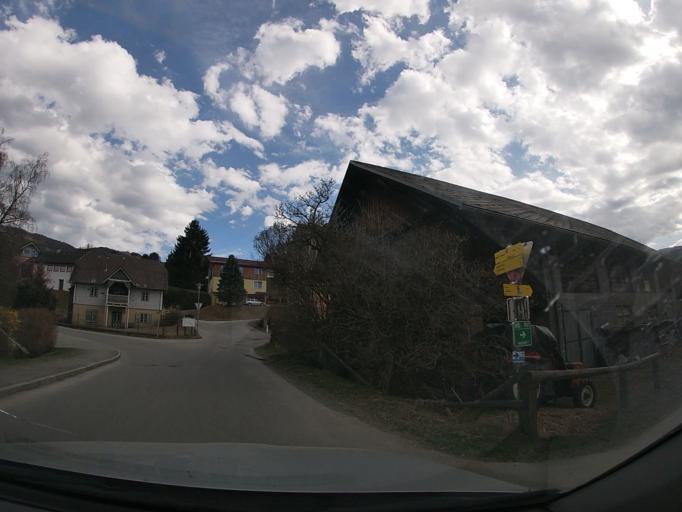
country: AT
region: Styria
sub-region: Politischer Bezirk Murau
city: Sankt Lambrecht
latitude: 47.0672
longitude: 14.2983
